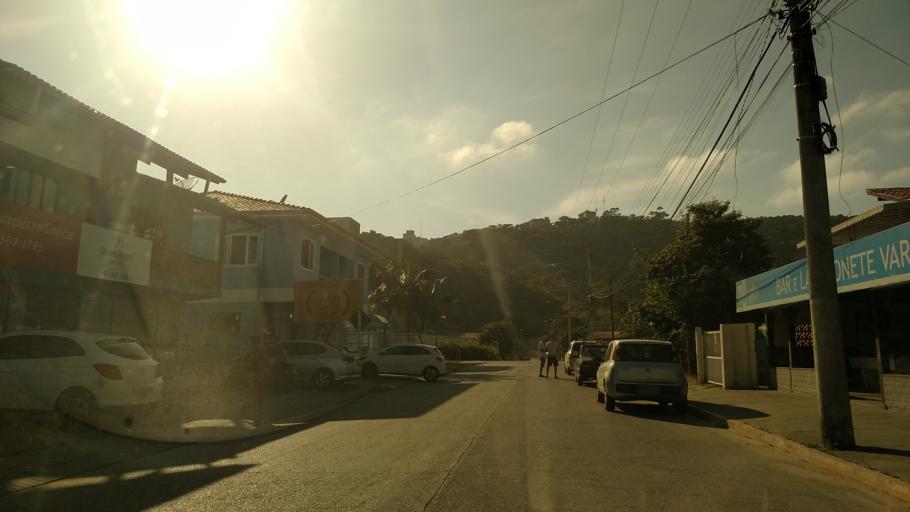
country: BR
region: Santa Catarina
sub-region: Porto Belo
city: Porto Belo
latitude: -27.1539
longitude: -48.5035
